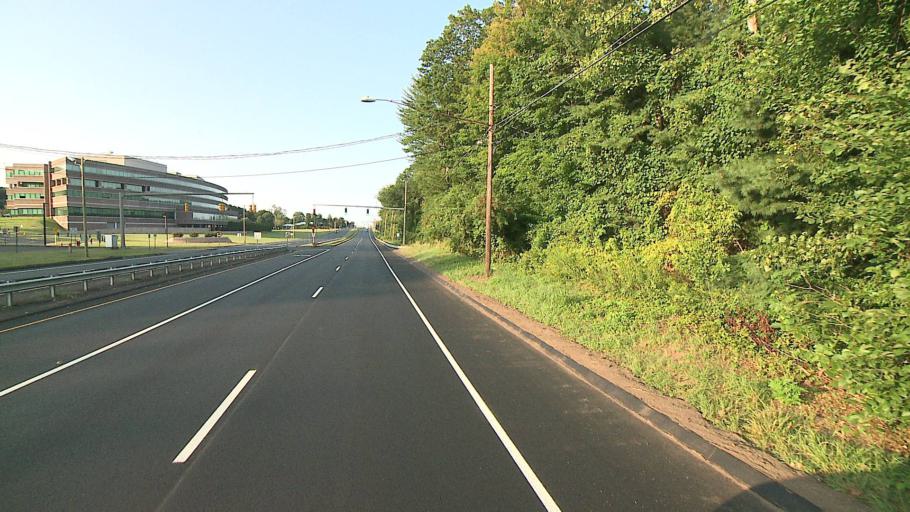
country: US
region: Connecticut
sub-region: Hartford County
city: Newington
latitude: 41.6756
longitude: -72.7147
